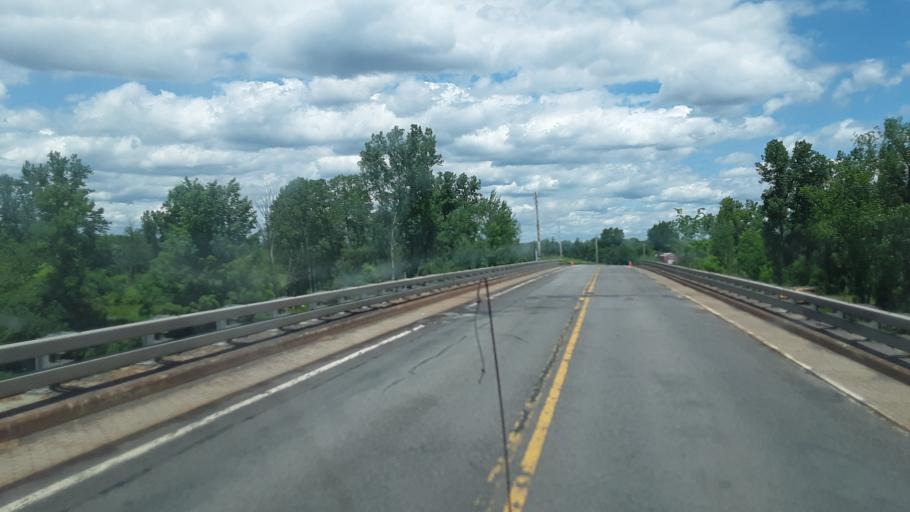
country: US
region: New York
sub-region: Madison County
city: Oneida
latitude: 43.2074
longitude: -75.5930
